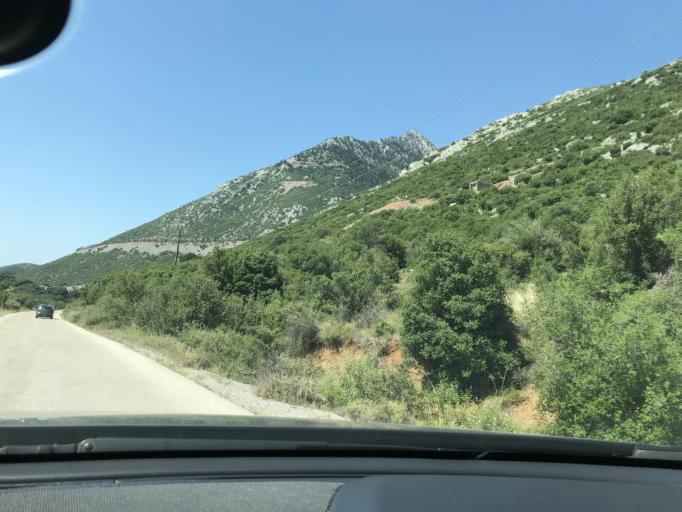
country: GR
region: Central Greece
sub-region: Nomos Voiotias
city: Distomo
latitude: 38.4801
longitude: 22.6862
